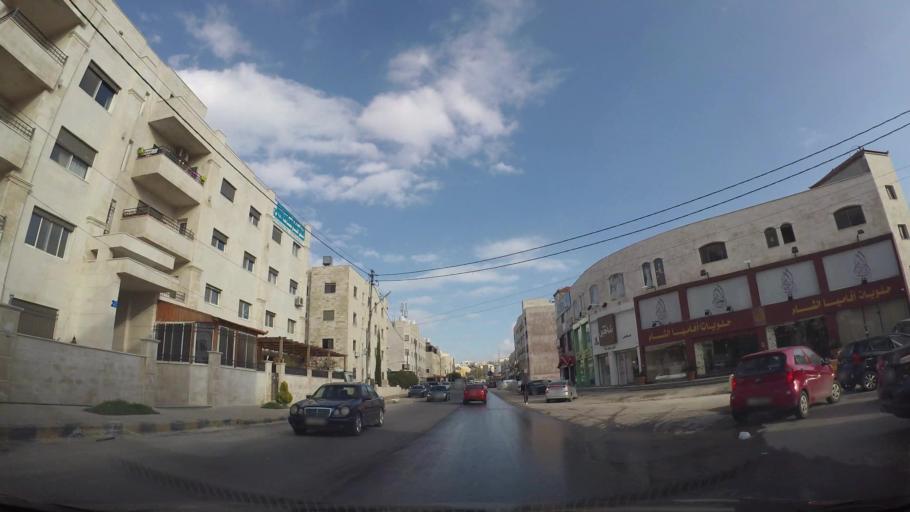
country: JO
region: Amman
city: Umm as Summaq
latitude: 31.9008
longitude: 35.8546
